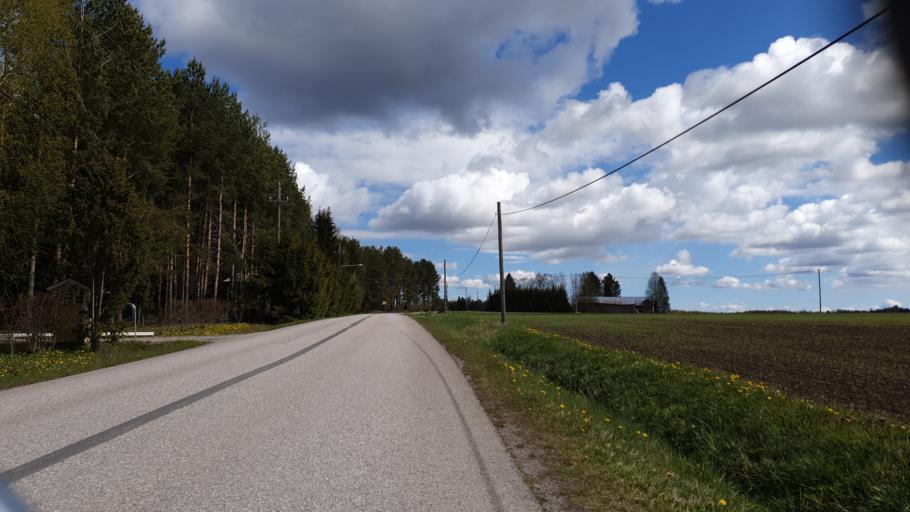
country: FI
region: Uusimaa
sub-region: Helsinki
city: Tuusula
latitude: 60.3948
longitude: 24.9175
